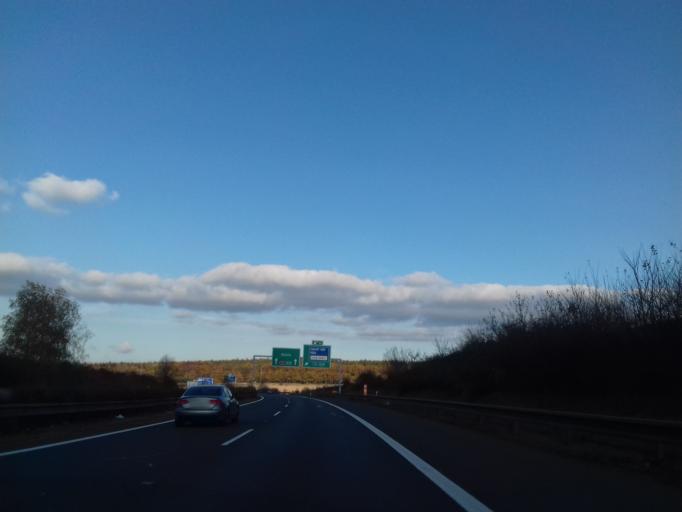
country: CZ
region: Plzensky
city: Stenovice
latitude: 49.6845
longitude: 13.4255
